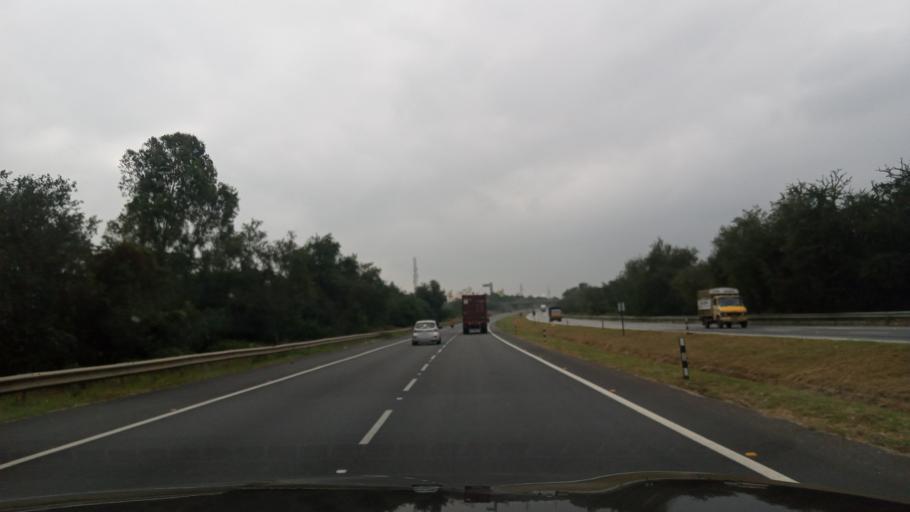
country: IN
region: Karnataka
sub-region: Bangalore Rural
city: Nelamangala
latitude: 13.0180
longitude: 77.4761
